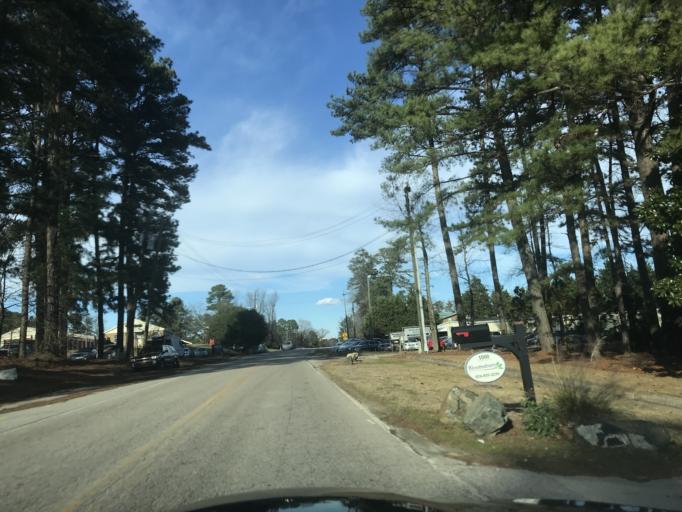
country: US
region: North Carolina
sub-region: Wake County
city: Cary
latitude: 35.7921
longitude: -78.7515
